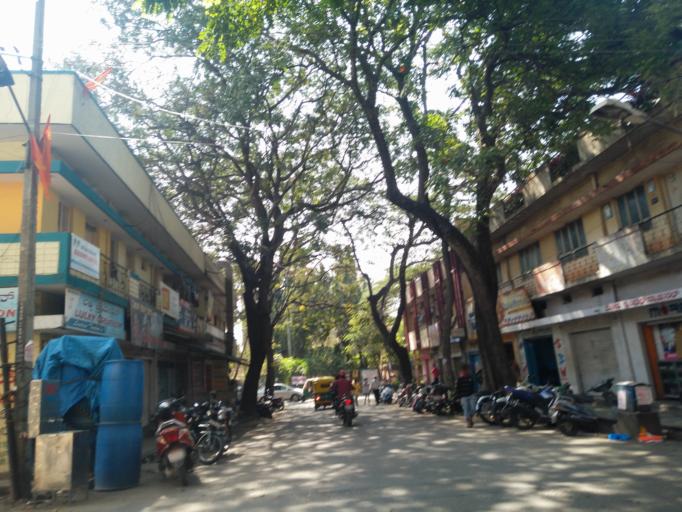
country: IN
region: Karnataka
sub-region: Bangalore Urban
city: Bangalore
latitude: 12.9706
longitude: 77.5436
